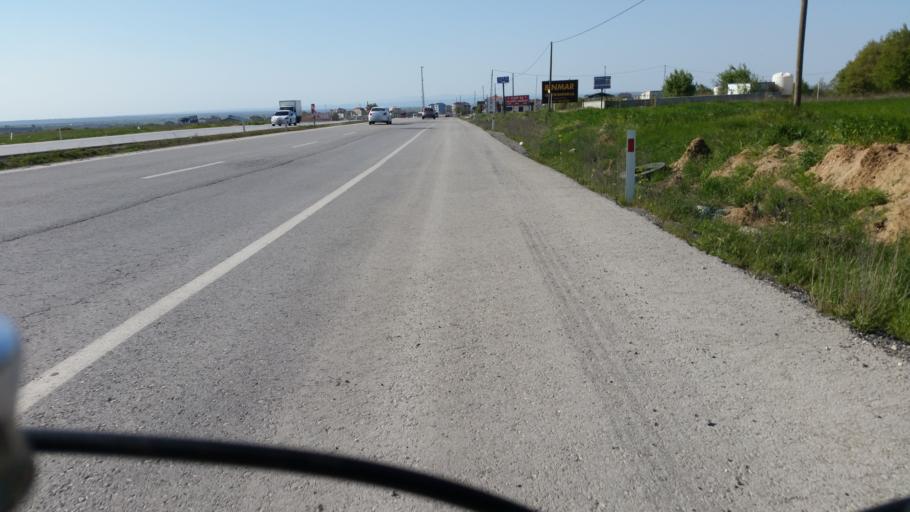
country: TR
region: Tekirdag
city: Cerkezkoey
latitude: 41.3480
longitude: 27.9597
